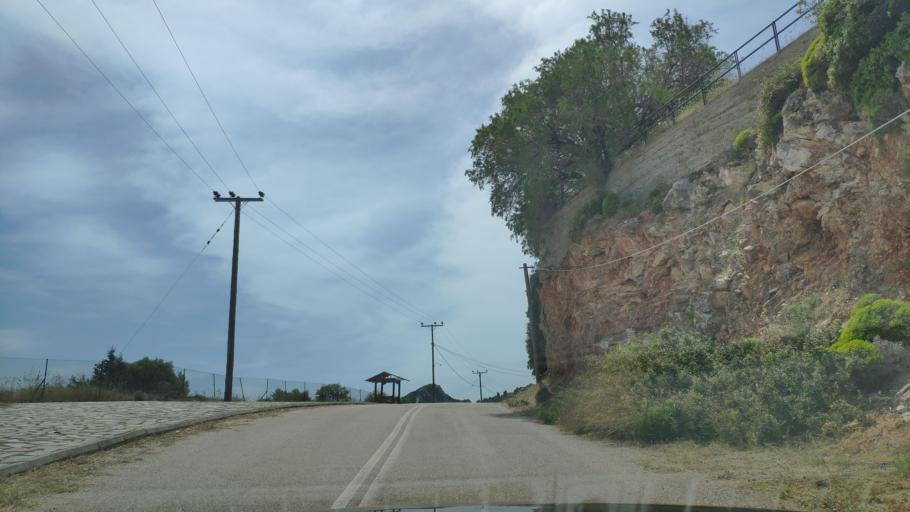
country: GR
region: Attica
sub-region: Nomarchia Anatolikis Attikis
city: Grammatiko
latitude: 38.2650
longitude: 23.9744
